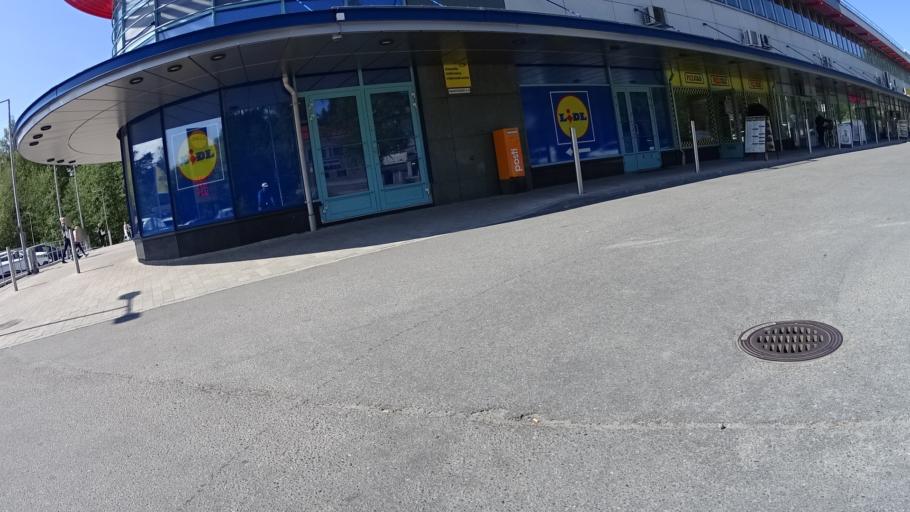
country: FI
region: Uusimaa
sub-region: Helsinki
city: Kilo
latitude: 60.1947
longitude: 24.7678
